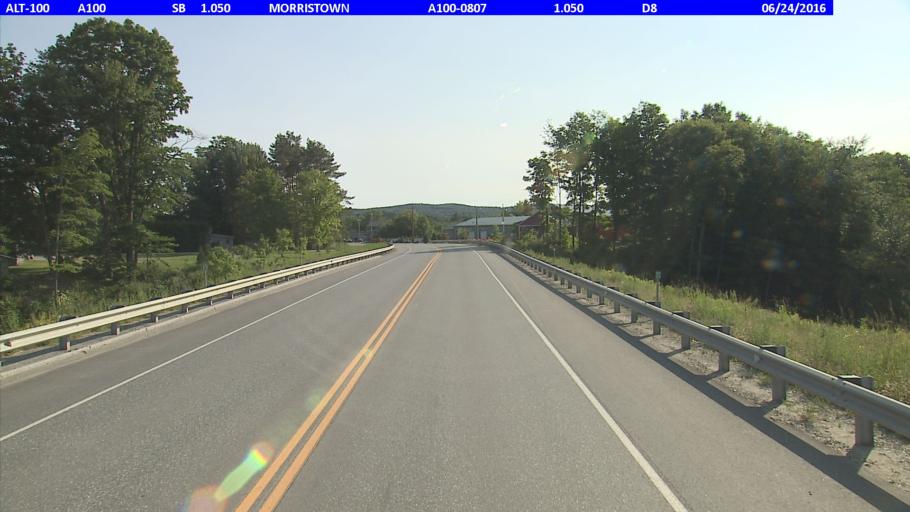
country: US
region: Vermont
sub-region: Lamoille County
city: Morrisville
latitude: 44.5705
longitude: -72.6010
